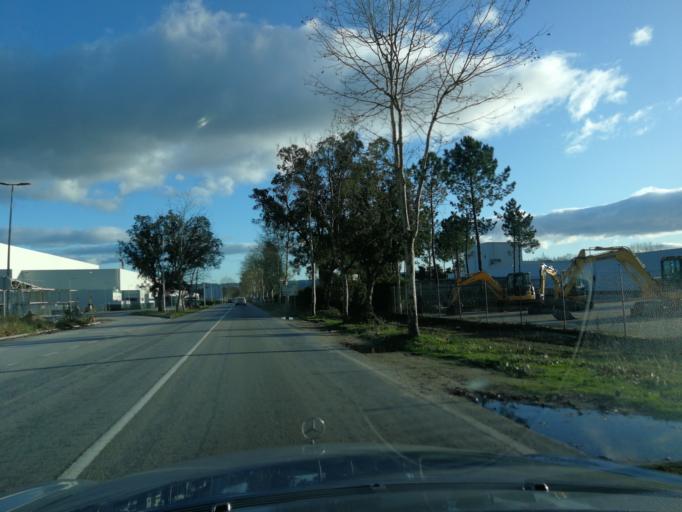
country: PT
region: Viana do Castelo
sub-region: Viana do Castelo
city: Darque
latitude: 41.6392
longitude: -8.7677
